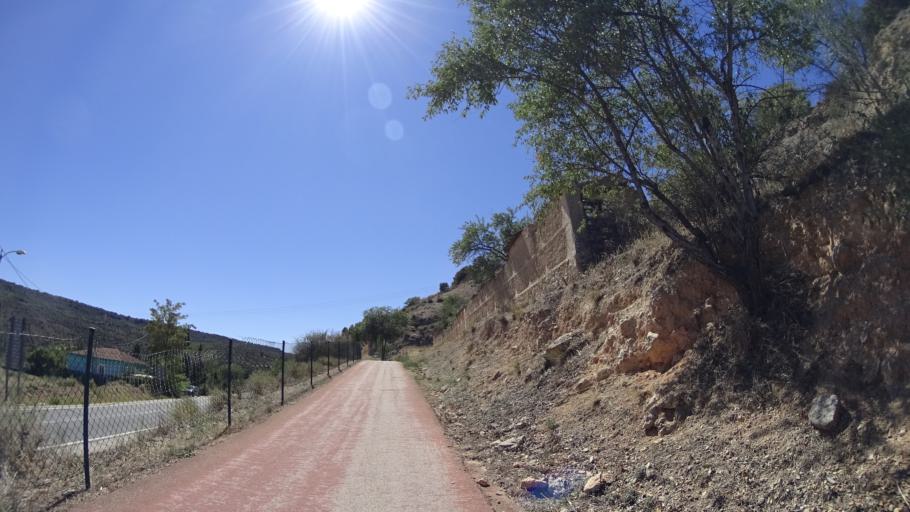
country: ES
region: Madrid
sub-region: Provincia de Madrid
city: Perales de Tajuna
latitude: 40.2328
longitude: -3.3580
